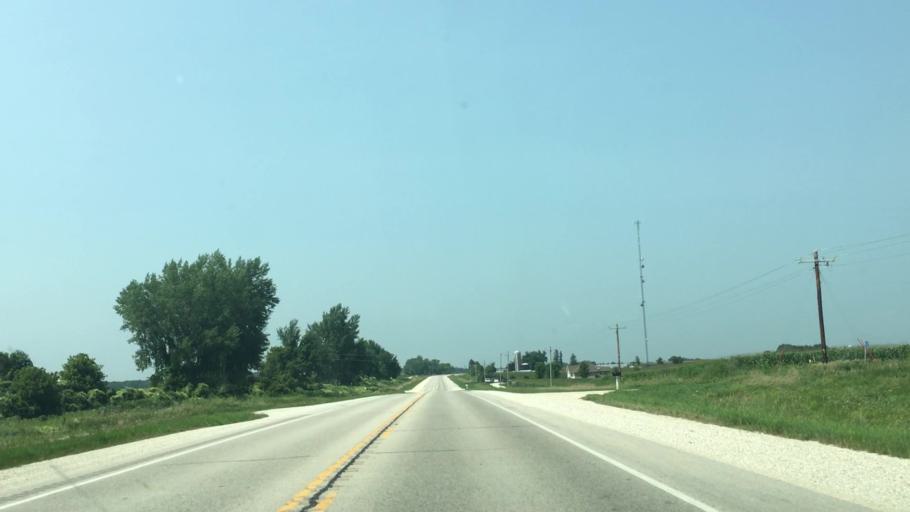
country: US
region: Iowa
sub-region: Winneshiek County
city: Decorah
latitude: 43.1964
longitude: -91.8738
